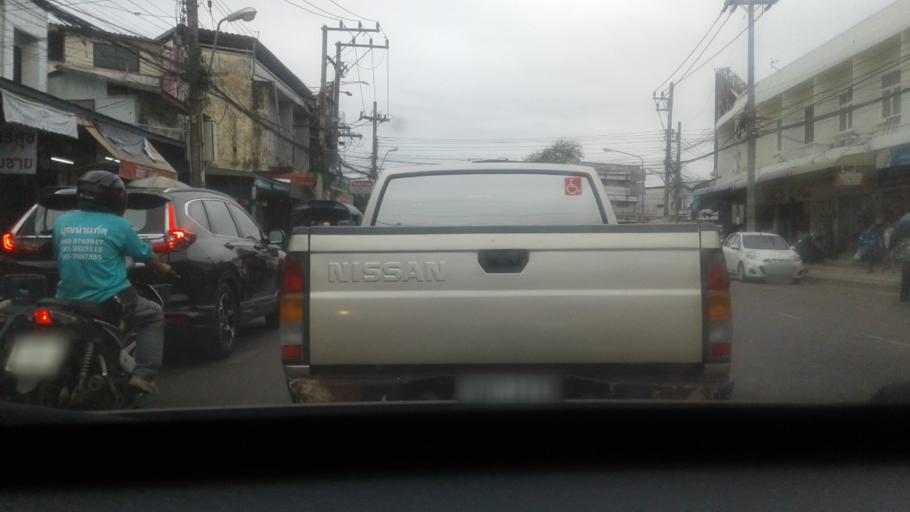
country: TH
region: Changwat Udon Thani
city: Udon Thani
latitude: 17.4012
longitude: 102.7940
